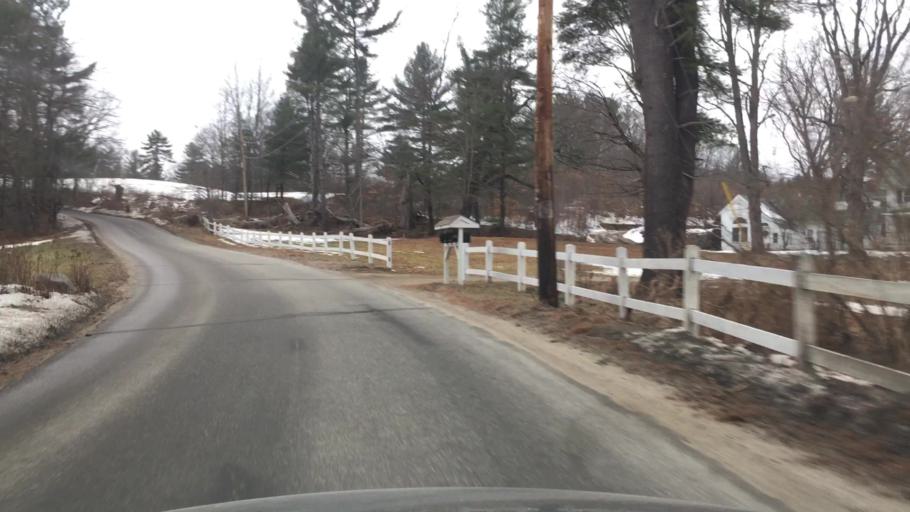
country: US
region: New Hampshire
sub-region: Hillsborough County
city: New Boston
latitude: 43.0066
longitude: -71.6656
